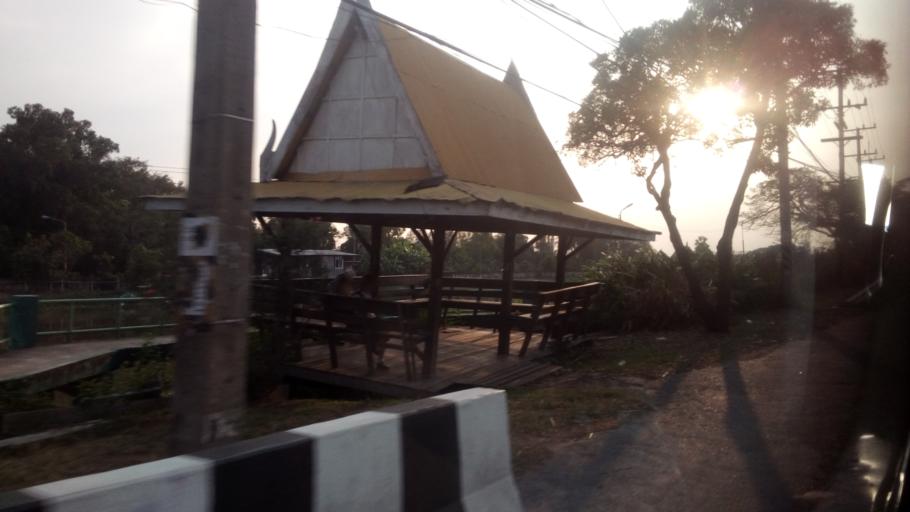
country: TH
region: Pathum Thani
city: Thanyaburi
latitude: 13.9980
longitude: 100.6777
